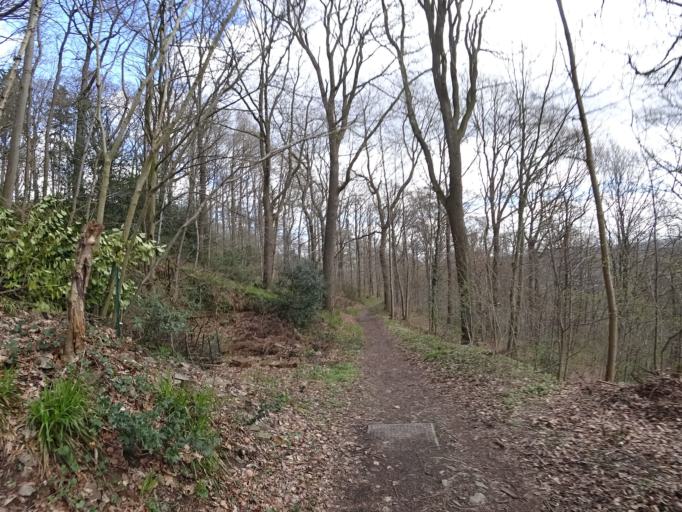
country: BE
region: Wallonia
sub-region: Province de Namur
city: Namur
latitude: 50.4518
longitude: 4.8518
